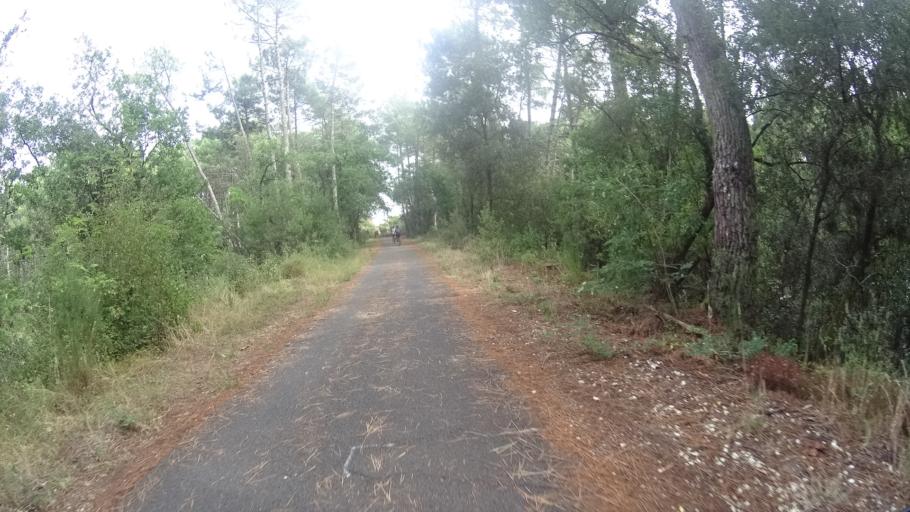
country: FR
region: Aquitaine
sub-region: Departement de la Gironde
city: Lacanau
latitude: 45.0047
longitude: -1.1383
